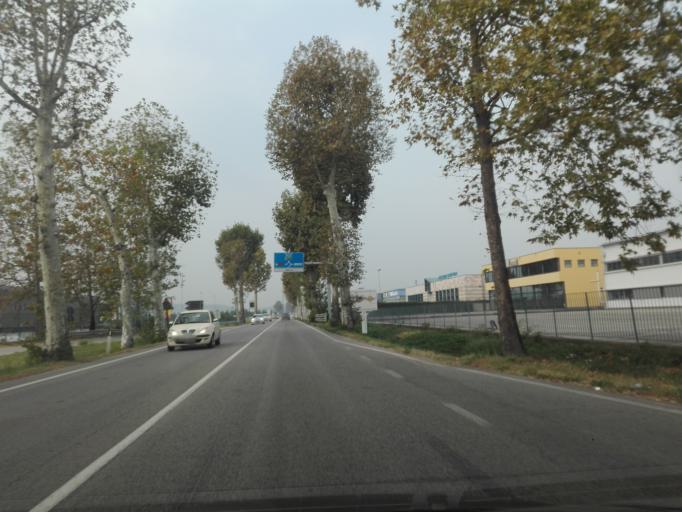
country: IT
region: Veneto
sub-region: Provincia di Verona
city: Lugagnano
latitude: 45.4463
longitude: 10.8691
